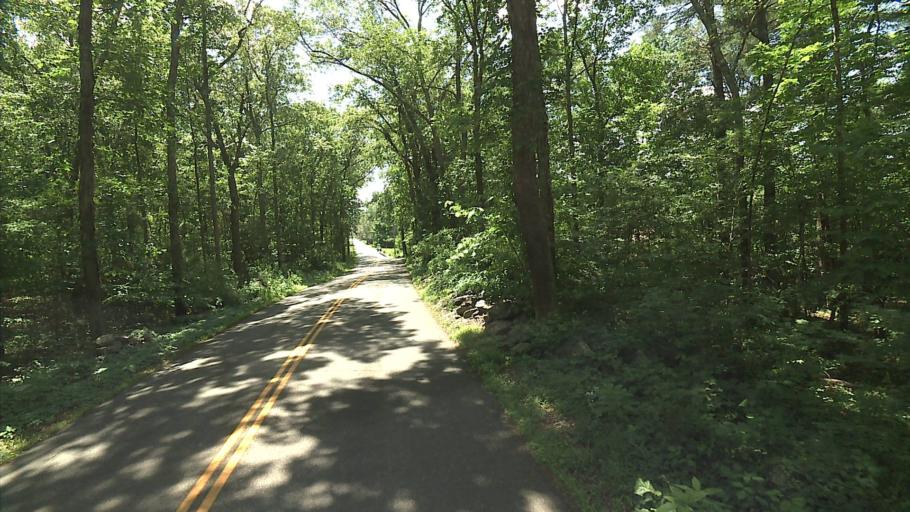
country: US
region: Connecticut
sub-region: New London County
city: Jewett City
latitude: 41.5894
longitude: -71.9018
